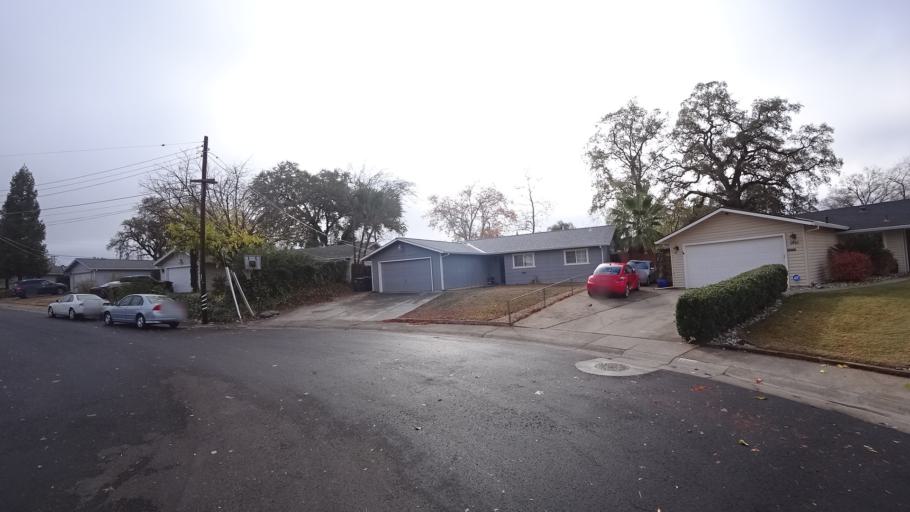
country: US
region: California
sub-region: Sacramento County
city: Antelope
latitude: 38.6930
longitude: -121.3079
